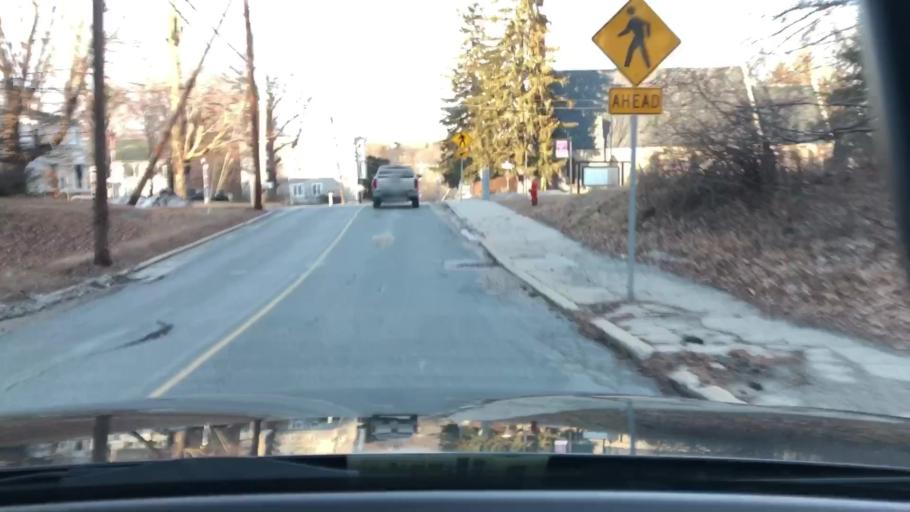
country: US
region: Massachusetts
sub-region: Worcester County
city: Millville
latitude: 42.0237
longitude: -71.5830
